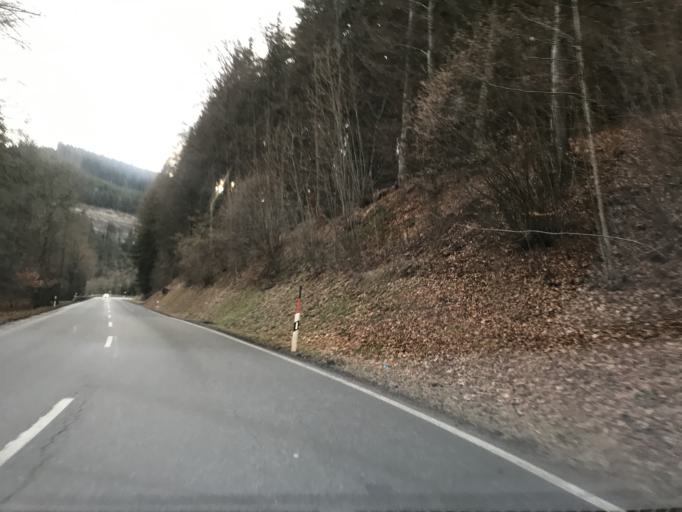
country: DE
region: Baden-Wuerttemberg
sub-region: Freiburg Region
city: Friedenweiler
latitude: 47.9055
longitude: 8.2414
